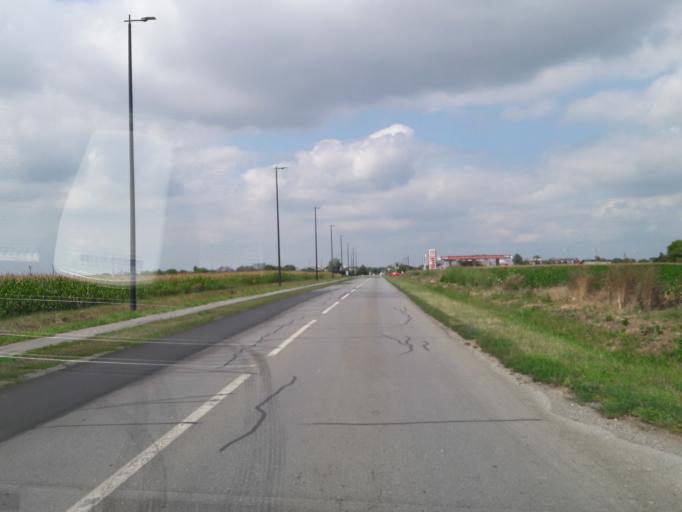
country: HR
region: Osjecko-Baranjska
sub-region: Grad Osijek
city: Osijek
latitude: 45.5335
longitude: 18.7178
